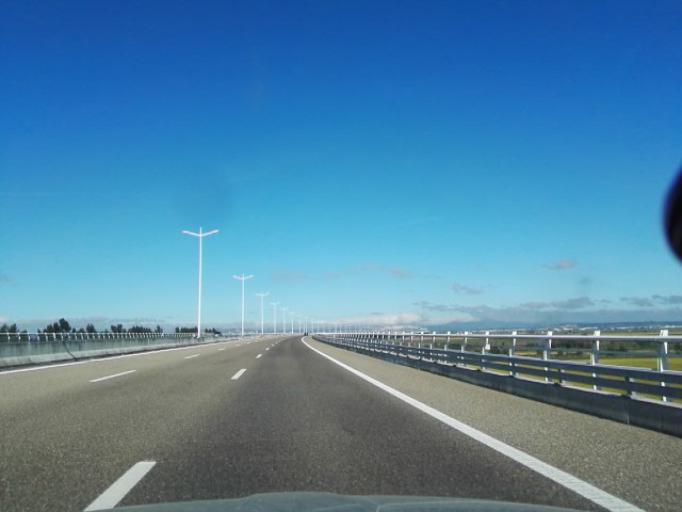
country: PT
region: Santarem
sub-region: Benavente
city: Samora Correia
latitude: 38.9716
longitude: -8.8738
